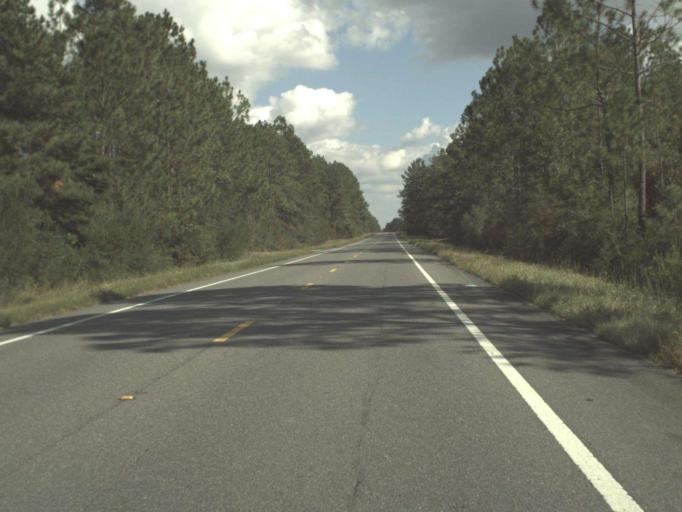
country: US
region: Florida
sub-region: Bay County
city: Laguna Beach
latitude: 30.4440
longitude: -85.8276
